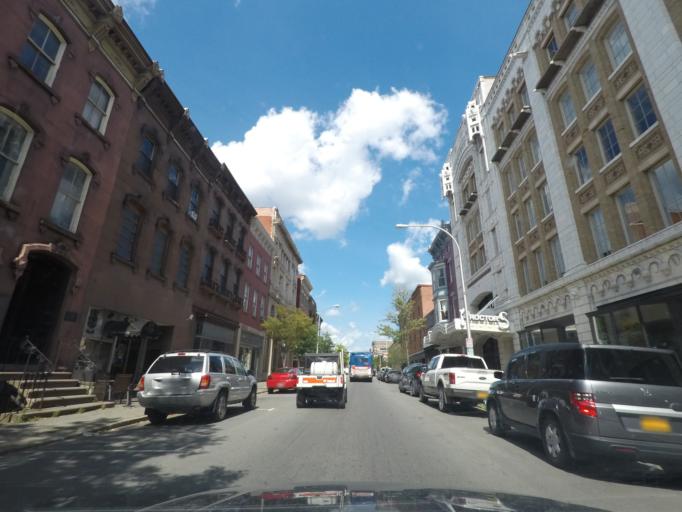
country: US
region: New York
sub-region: Rensselaer County
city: Troy
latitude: 42.7303
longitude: -73.6892
